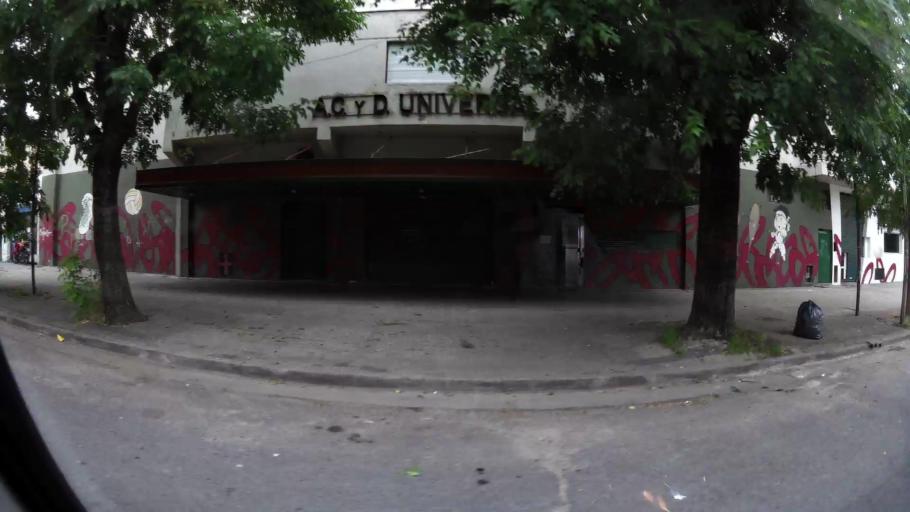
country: AR
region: Buenos Aires
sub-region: Partido de La Plata
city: La Plata
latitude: -34.9358
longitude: -57.9628
